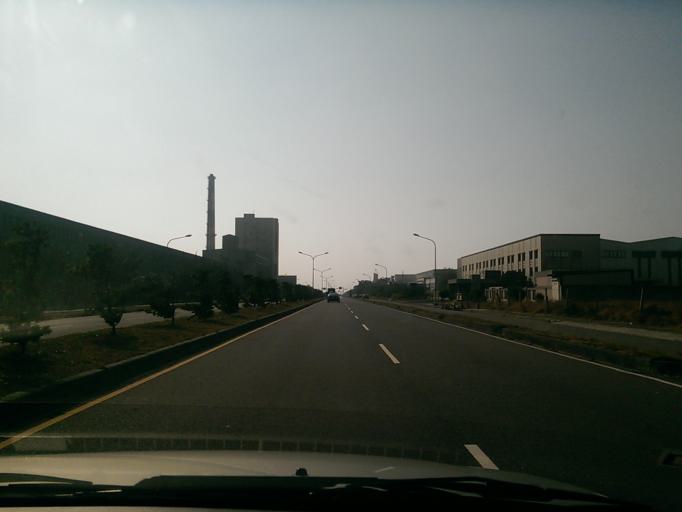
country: TW
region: Taiwan
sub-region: Changhua
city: Chang-hua
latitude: 24.0775
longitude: 120.4039
